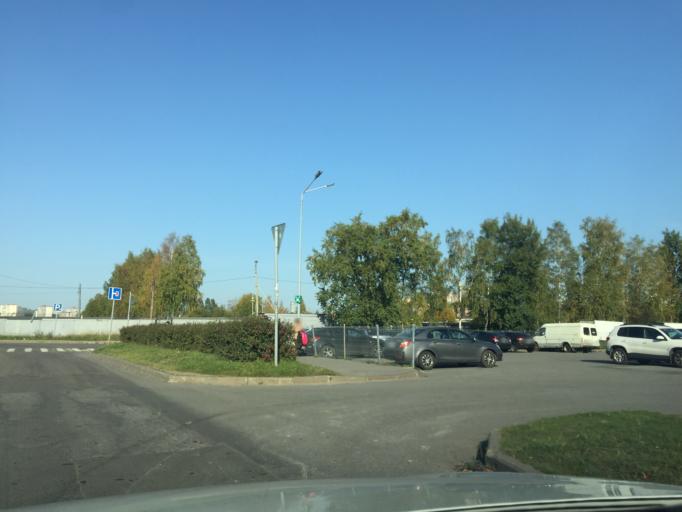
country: RU
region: Leningrad
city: Murino
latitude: 60.0319
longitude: 30.4333
